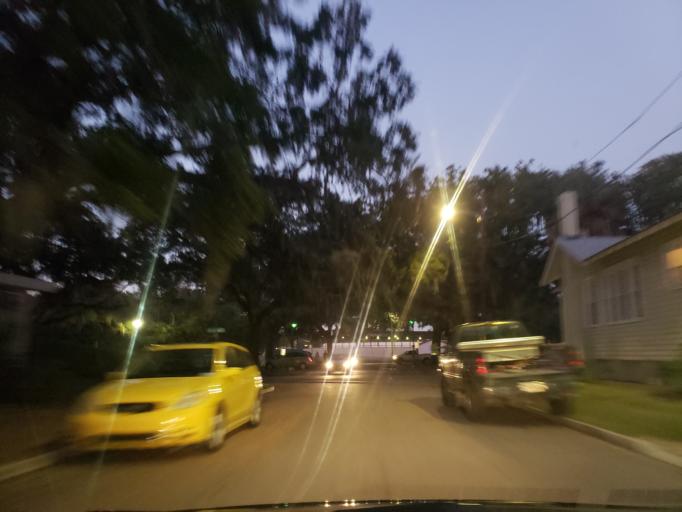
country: US
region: Georgia
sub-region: Chatham County
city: Thunderbolt
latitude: 32.0427
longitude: -81.0797
